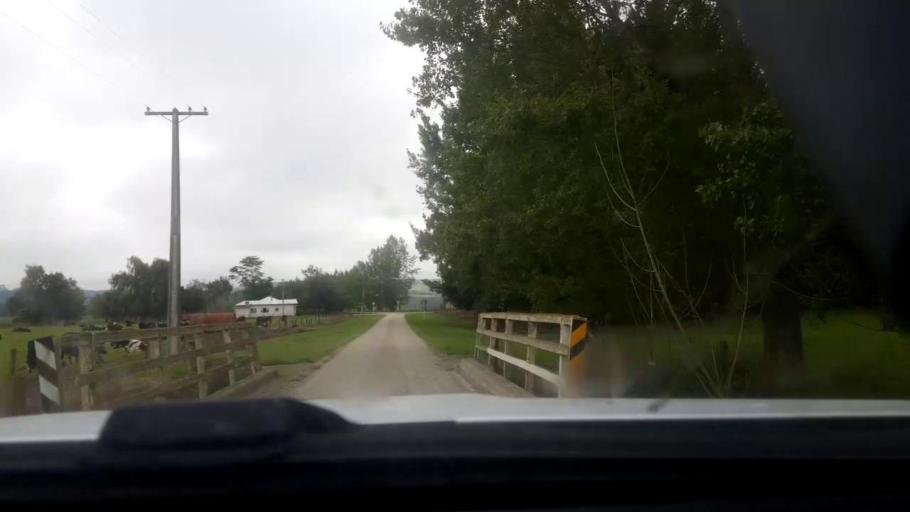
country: NZ
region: Canterbury
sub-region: Timaru District
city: Pleasant Point
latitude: -44.2084
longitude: 171.1125
